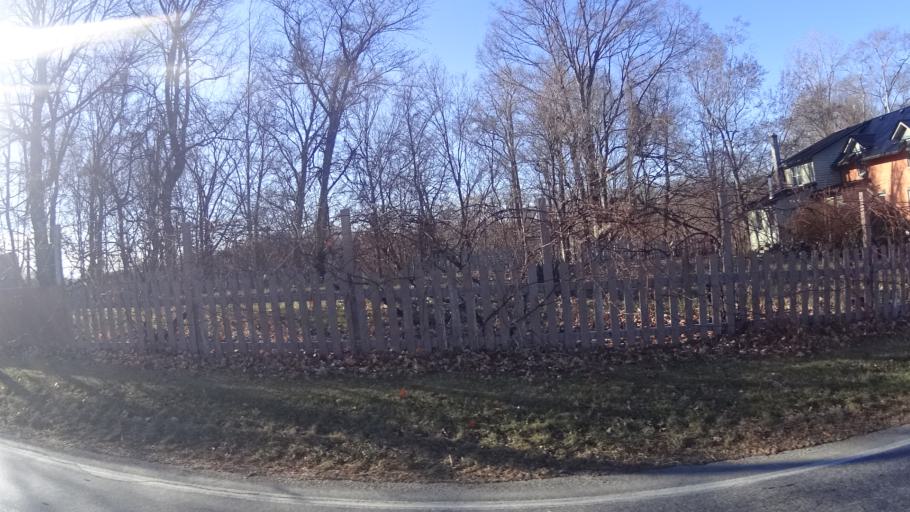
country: US
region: Ohio
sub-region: Lorain County
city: South Amherst
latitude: 41.3667
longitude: -82.3043
